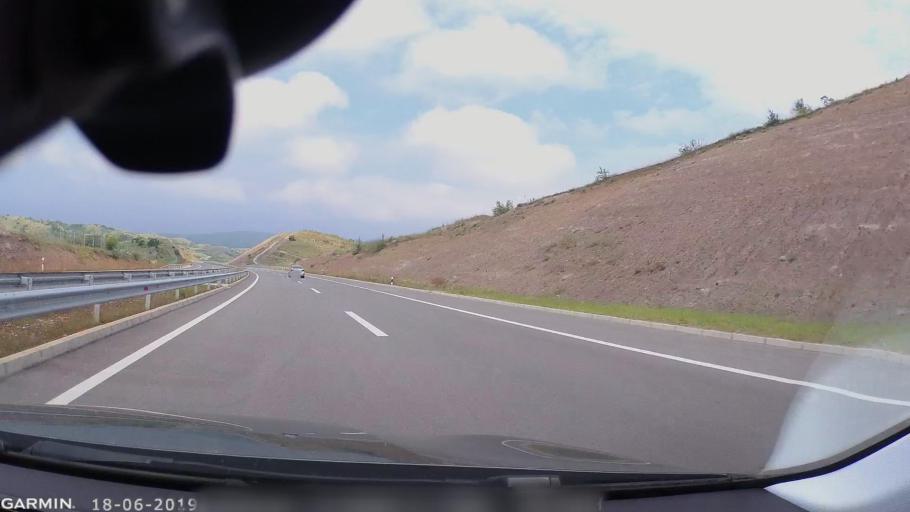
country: MK
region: Sveti Nikole
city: Gorobinci
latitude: 41.9266
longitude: 21.8340
